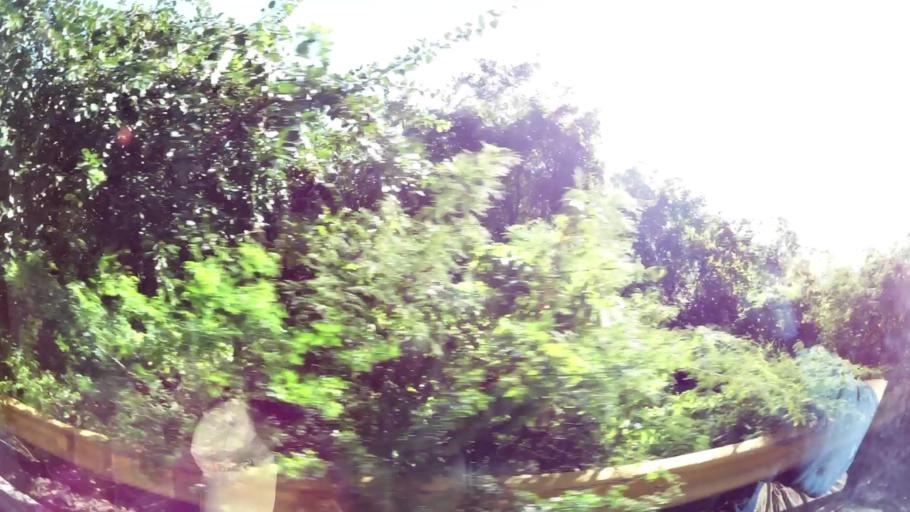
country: VG
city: Tortola
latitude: 18.4138
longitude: -64.5930
